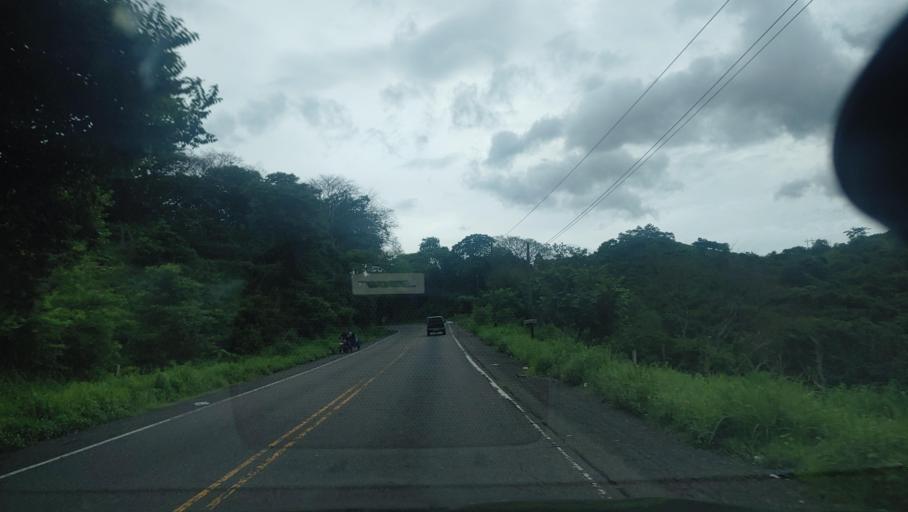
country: HN
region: Choluteca
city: Santa Ana de Yusguare
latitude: 13.3714
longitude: -87.0754
